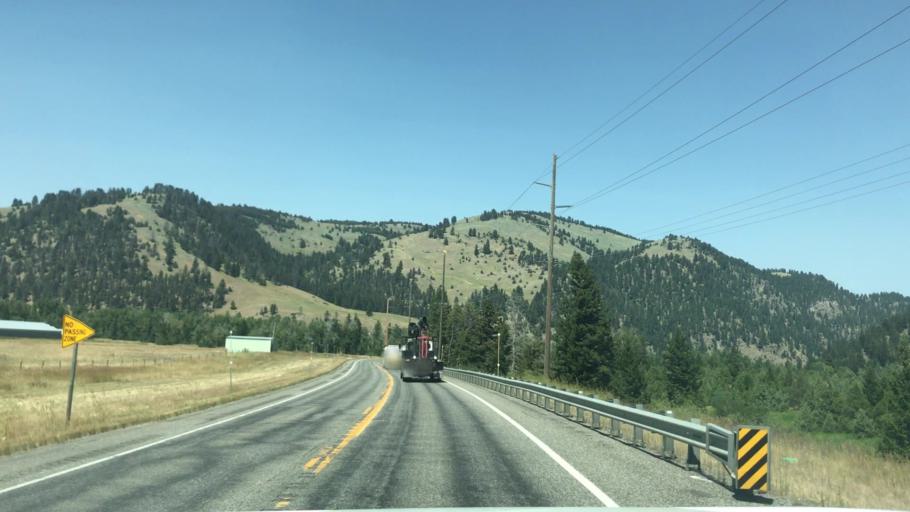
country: US
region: Montana
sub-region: Gallatin County
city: Four Corners
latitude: 45.4888
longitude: -111.2712
